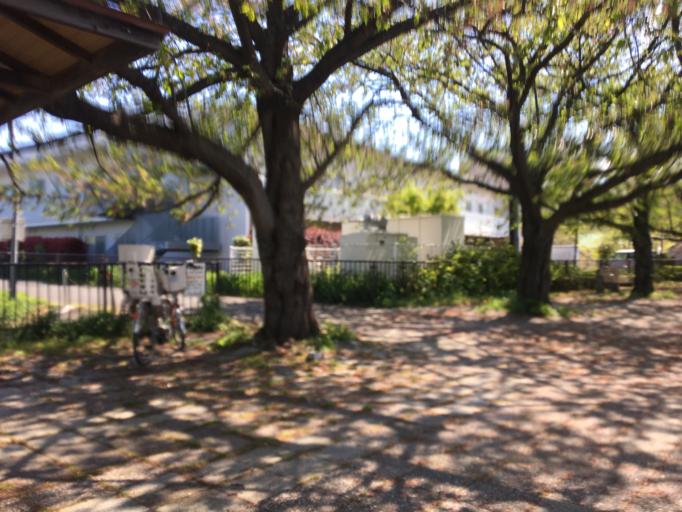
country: JP
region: Saitama
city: Wako
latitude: 35.8020
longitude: 139.6309
